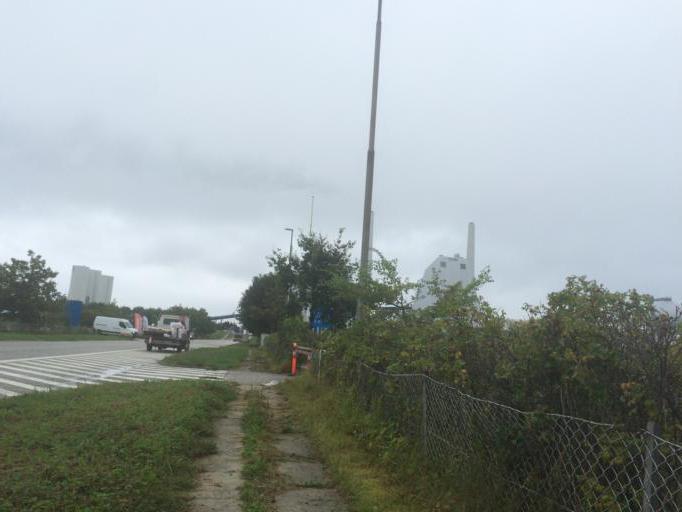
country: DK
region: Capital Region
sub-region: Hvidovre Kommune
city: Hvidovre
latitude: 55.6077
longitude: 12.4821
